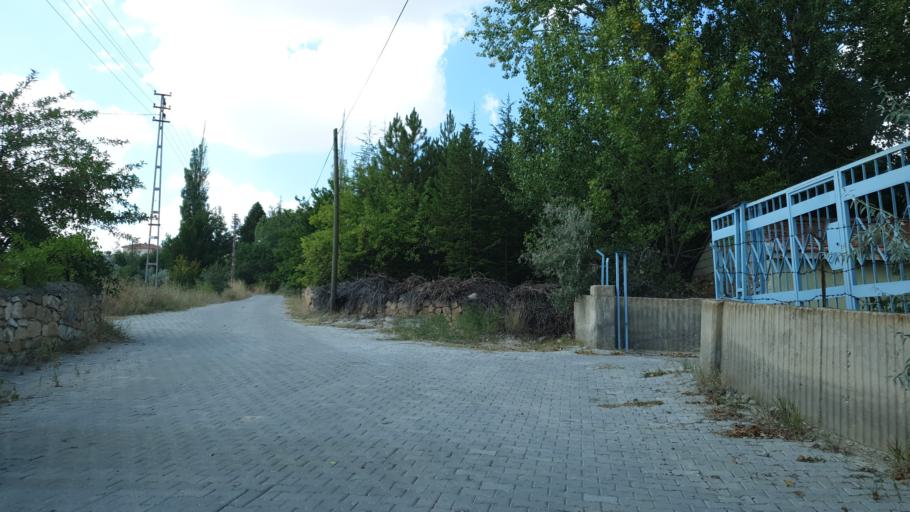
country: TR
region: Kayseri
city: Felahiye
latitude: 39.1148
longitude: 35.6097
